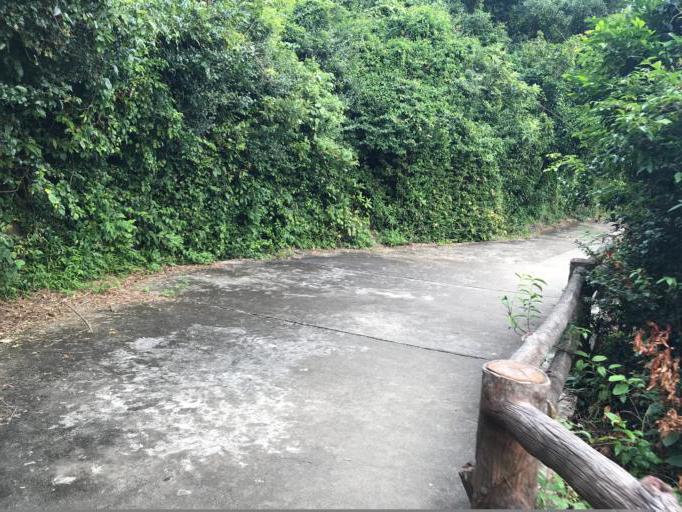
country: VN
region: Hai Phong
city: Cat Ba
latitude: 20.7147
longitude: 107.0524
